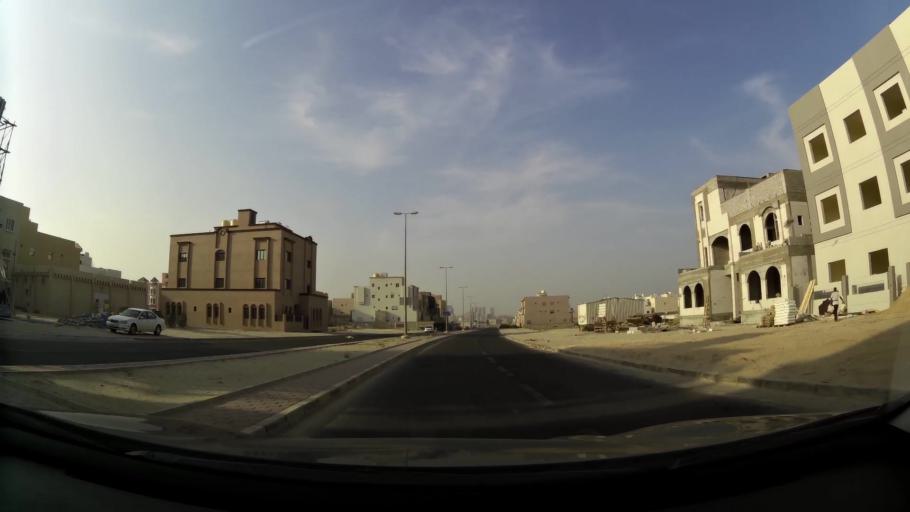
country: KW
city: Al Funaytis
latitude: 29.2329
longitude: 48.0887
